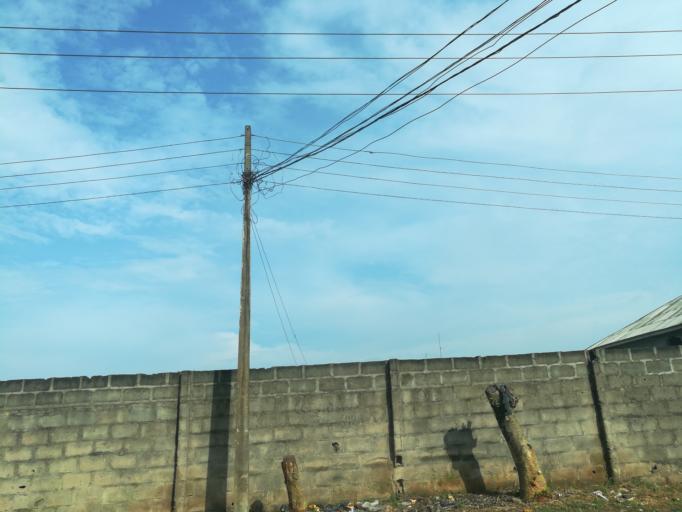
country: NG
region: Lagos
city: Ojota
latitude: 6.6031
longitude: 3.4201
